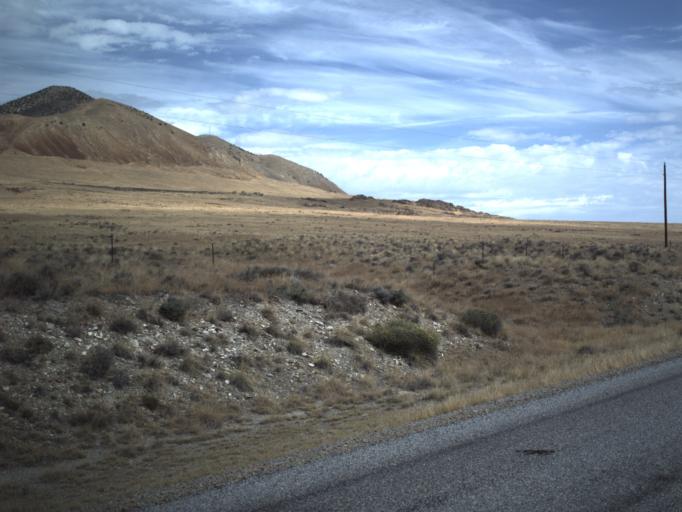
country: US
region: Utah
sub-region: Tooele County
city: Wendover
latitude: 41.4484
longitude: -113.6768
